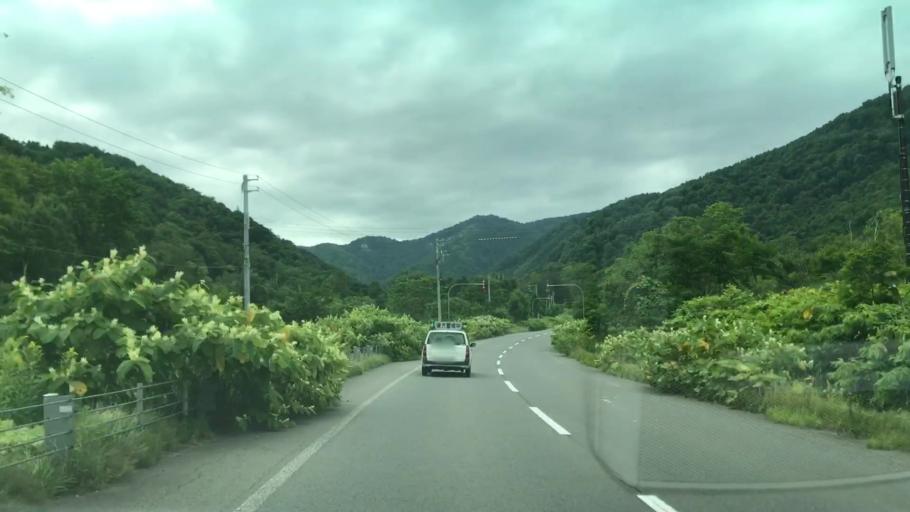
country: JP
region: Hokkaido
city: Yoichi
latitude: 43.0262
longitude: 140.8665
